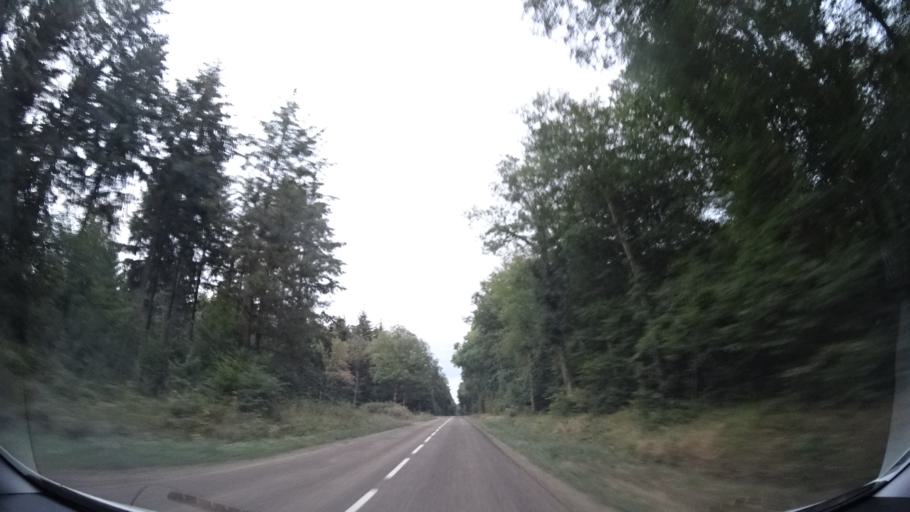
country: FR
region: Bourgogne
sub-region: Departement de l'Yonne
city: Aillant-sur-Tholon
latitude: 47.9276
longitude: 3.2814
